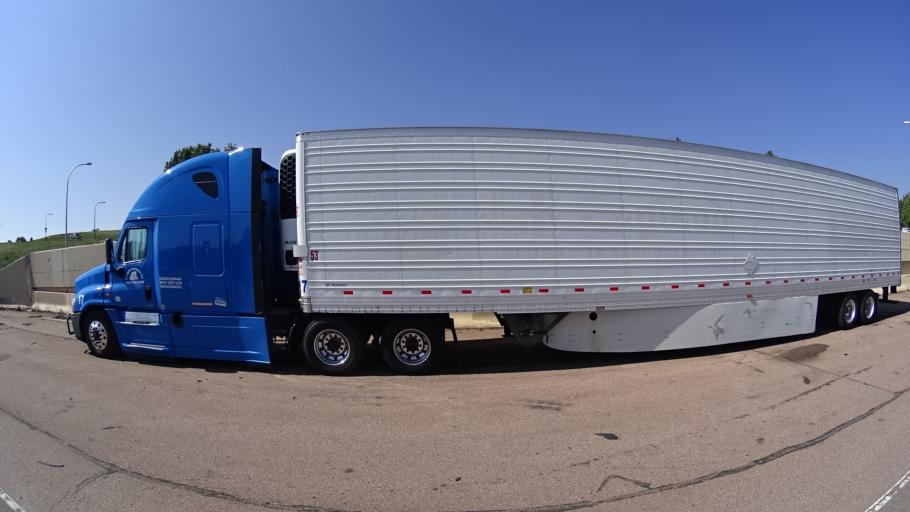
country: US
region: Colorado
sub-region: El Paso County
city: Stratmoor
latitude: 38.8169
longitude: -104.7721
